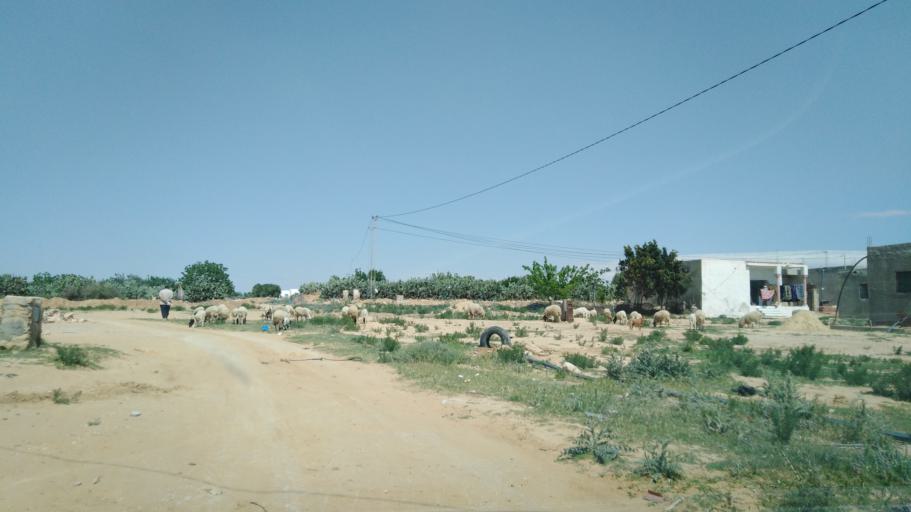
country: TN
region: Safaqis
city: Sfax
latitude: 34.7635
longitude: 10.5213
